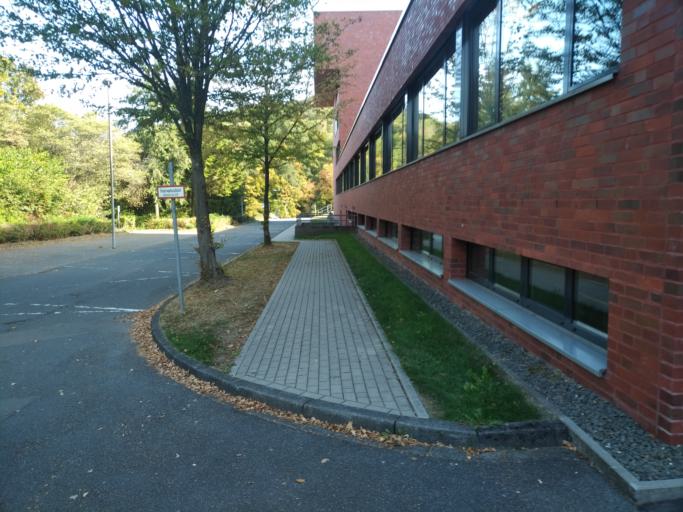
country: DE
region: North Rhine-Westphalia
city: Wiehl
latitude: 50.9822
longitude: 7.5470
